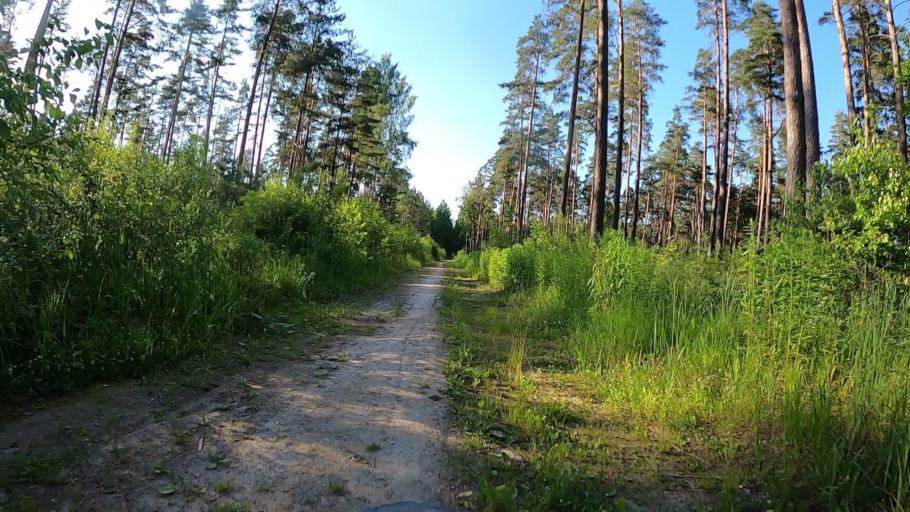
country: LV
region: Stopini
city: Ulbroka
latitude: 56.9256
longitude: 24.2349
